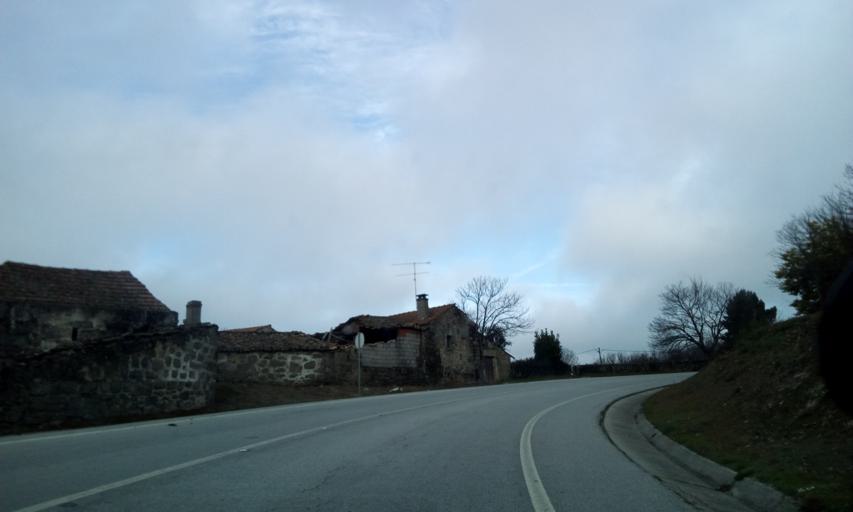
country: PT
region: Guarda
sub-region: Aguiar da Beira
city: Aguiar da Beira
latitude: 40.7261
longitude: -7.4960
